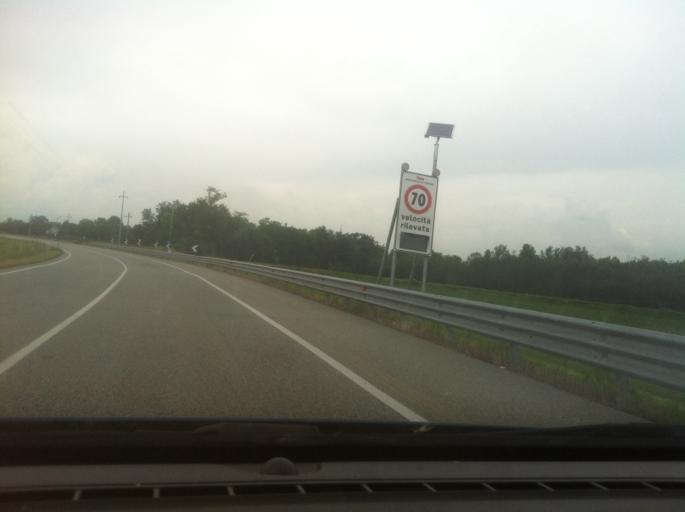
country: IT
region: Piedmont
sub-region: Provincia di Torino
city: Brandizzo
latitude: 45.2050
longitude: 7.8310
